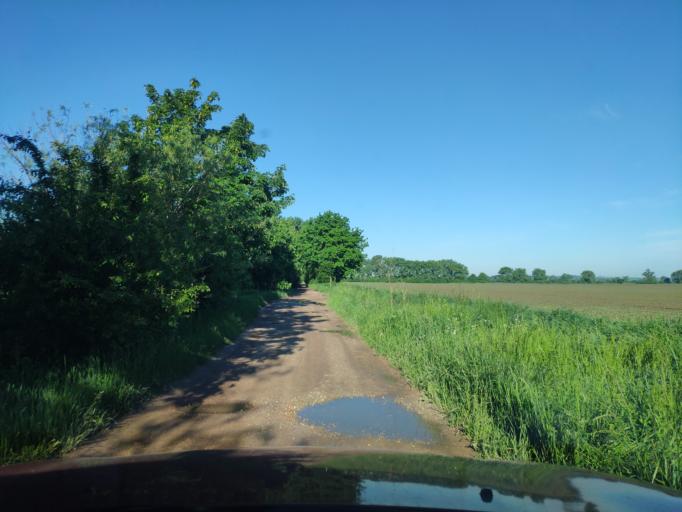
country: SK
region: Nitriansky
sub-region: Okres Nitra
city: Nitra
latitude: 48.2169
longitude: 18.1770
